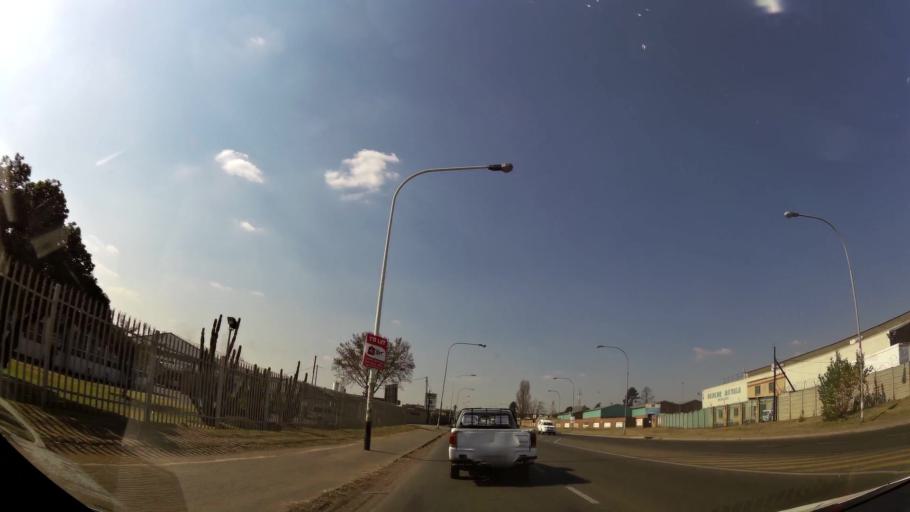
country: ZA
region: Gauteng
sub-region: Ekurhuleni Metropolitan Municipality
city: Boksburg
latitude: -26.2087
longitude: 28.2797
